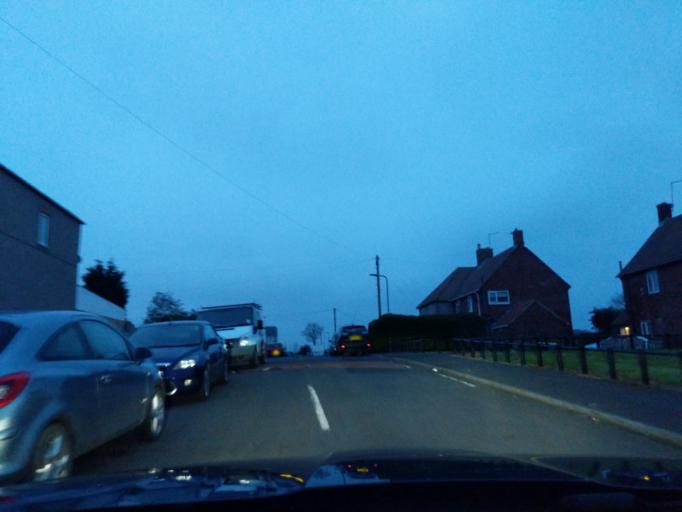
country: GB
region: England
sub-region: Northumberland
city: Lynemouth
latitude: 55.2140
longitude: -1.5458
